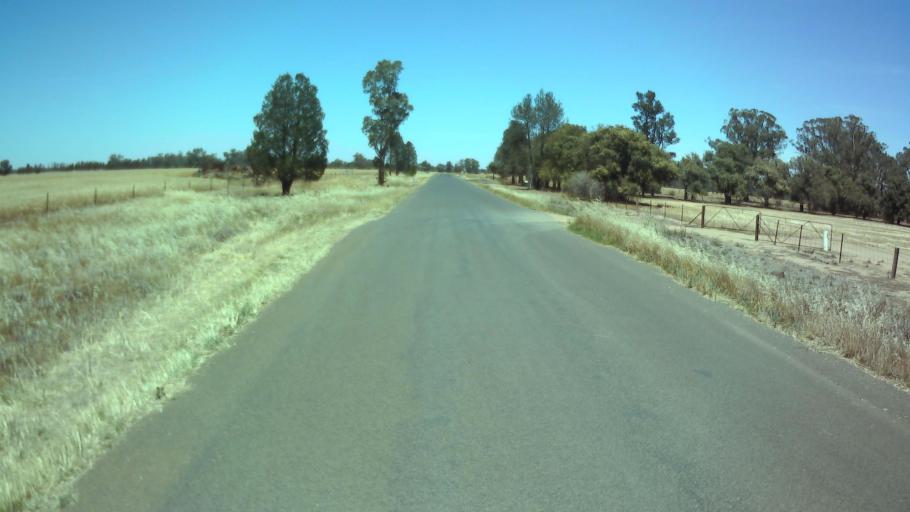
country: AU
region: New South Wales
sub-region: Weddin
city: Grenfell
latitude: -34.0308
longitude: 147.7907
